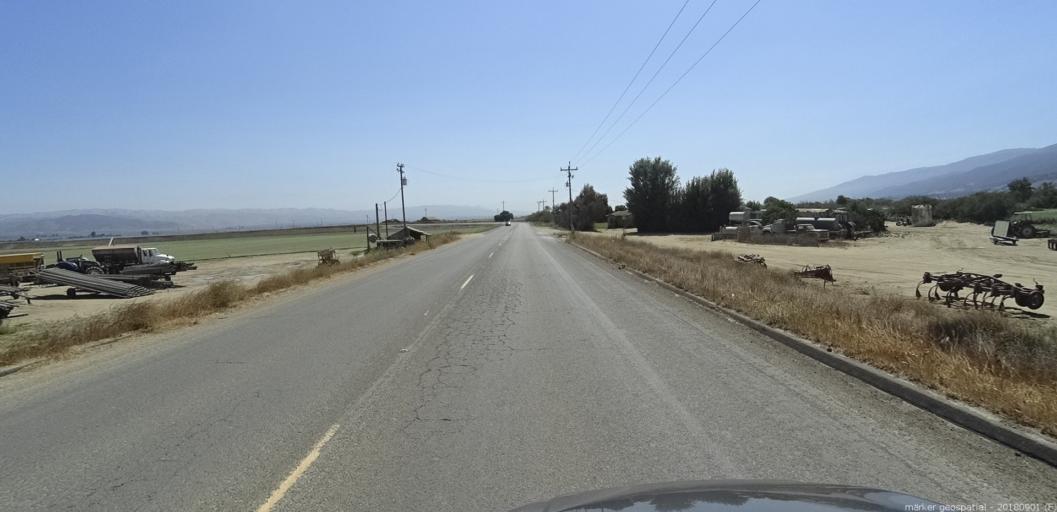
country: US
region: California
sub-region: Monterey County
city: Chualar
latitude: 36.5543
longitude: -121.5453
